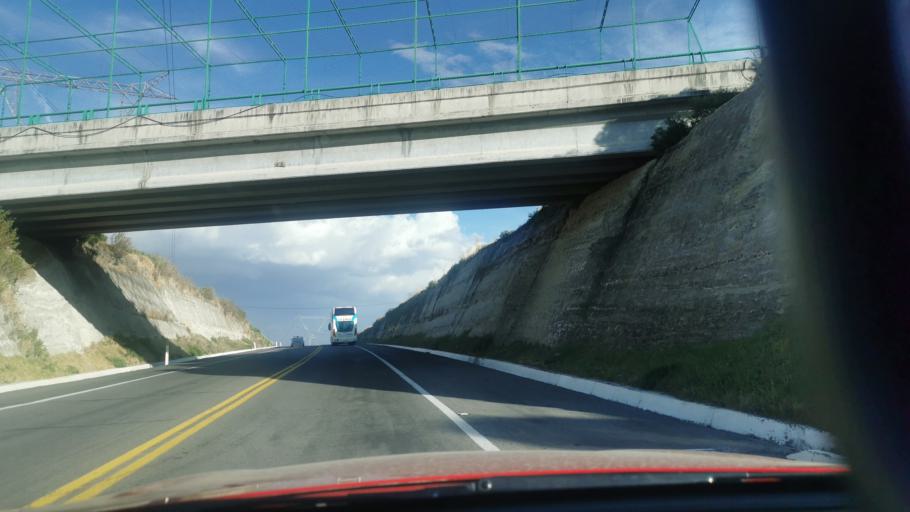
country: MX
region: Mexico
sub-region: Almoloya de Juarez
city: San Pedro de la Hortaliza (Ejido Almoloyan)
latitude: 19.3778
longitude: -99.8480
